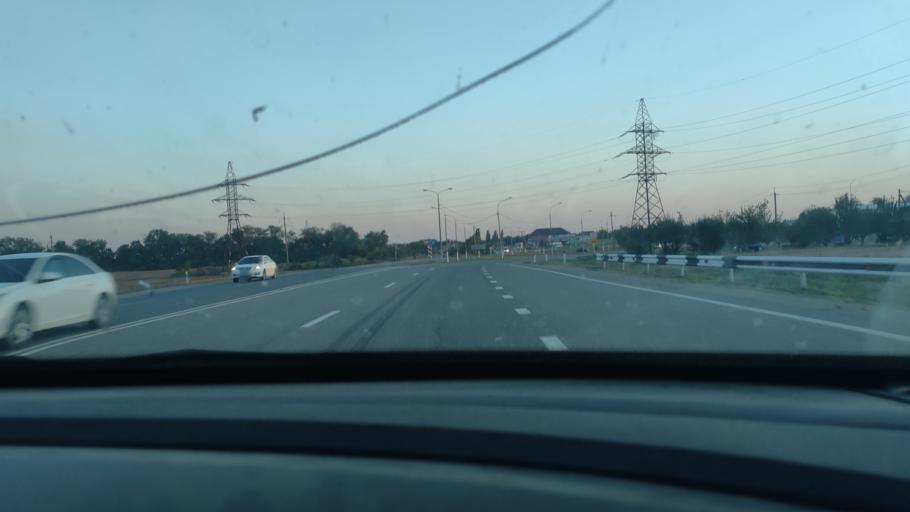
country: RU
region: Krasnodarskiy
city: Timashevsk
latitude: 45.6122
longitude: 38.9871
